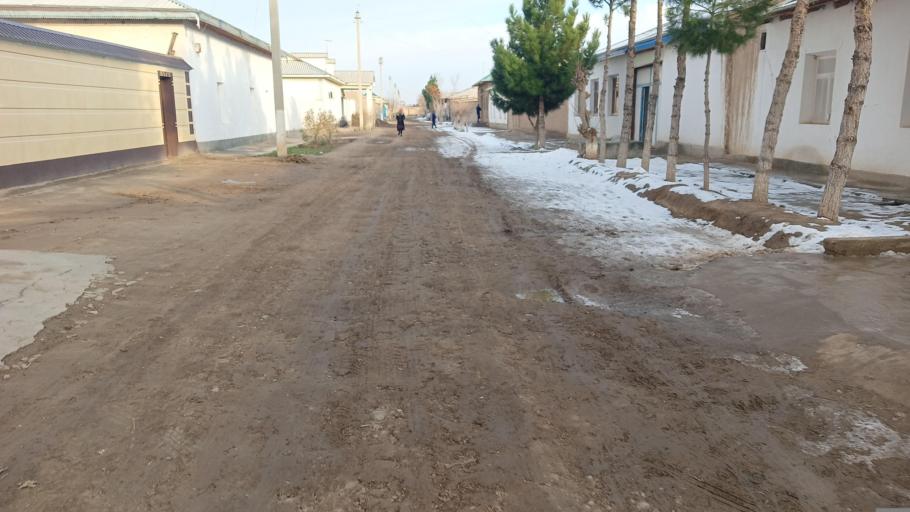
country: UZ
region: Qashqadaryo
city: Yangi Mirishkor
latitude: 38.8926
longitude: 65.3059
